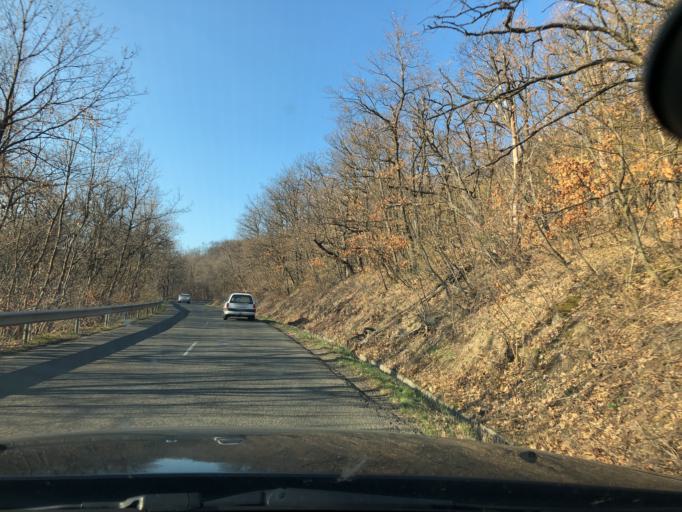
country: HU
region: Nograd
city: Paszto
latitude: 47.9253
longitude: 19.6294
